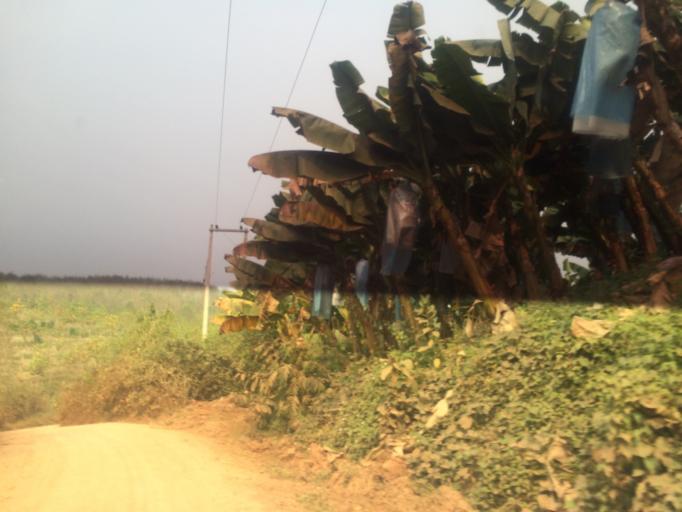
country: LA
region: Loungnamtha
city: Muang Nale
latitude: 20.4194
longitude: 101.6990
